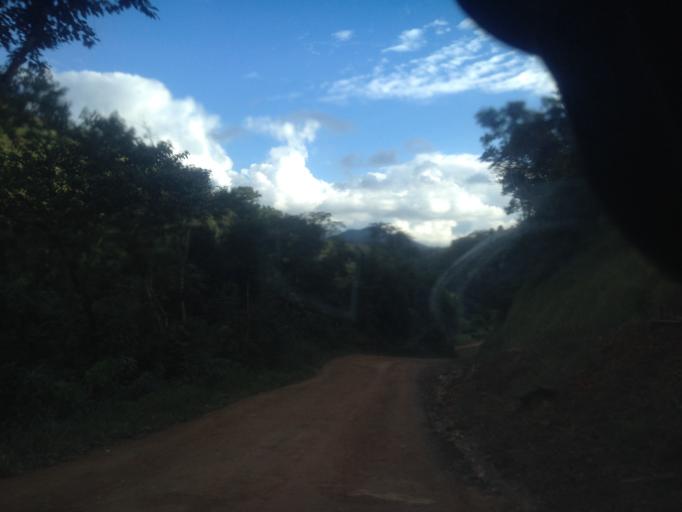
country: BR
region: Rio de Janeiro
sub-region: Quatis
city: Quatis
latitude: -22.2309
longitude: -44.2556
